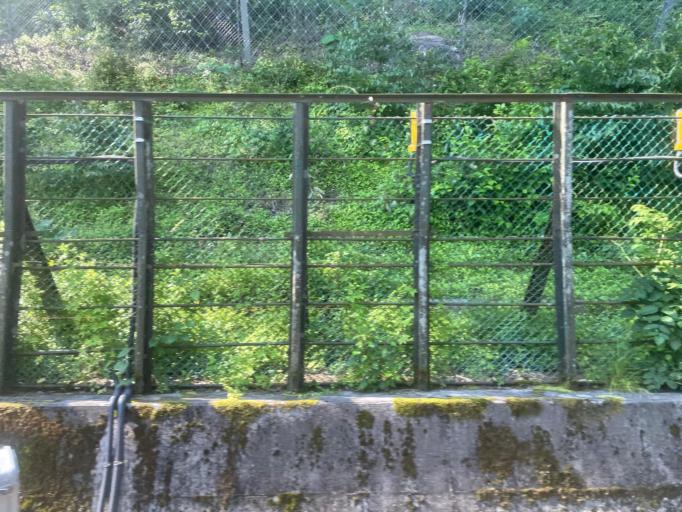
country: JP
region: Saitama
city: Chichibu
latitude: 35.9756
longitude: 139.1302
